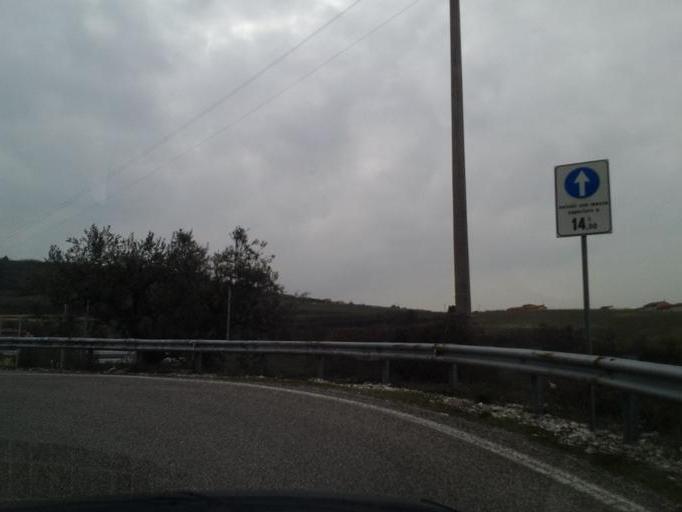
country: IT
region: Veneto
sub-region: Provincia di Verona
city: Montorio
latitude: 45.4903
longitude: 11.0789
